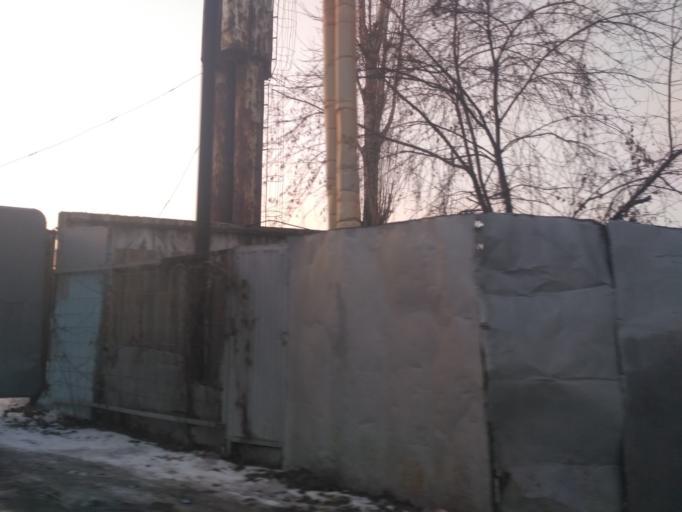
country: KZ
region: Almaty Qalasy
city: Almaty
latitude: 43.2672
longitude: 76.8621
